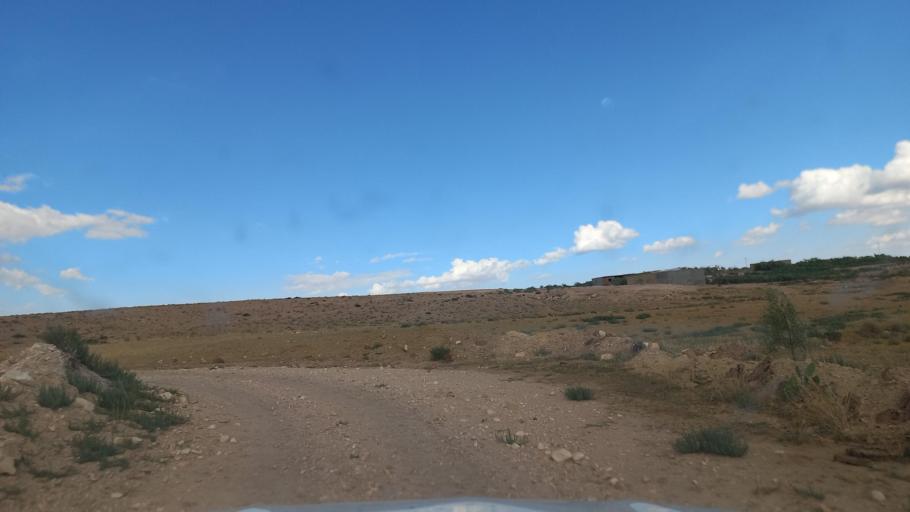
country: TN
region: Al Qasrayn
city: Sbiba
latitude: 35.4019
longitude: 9.0099
